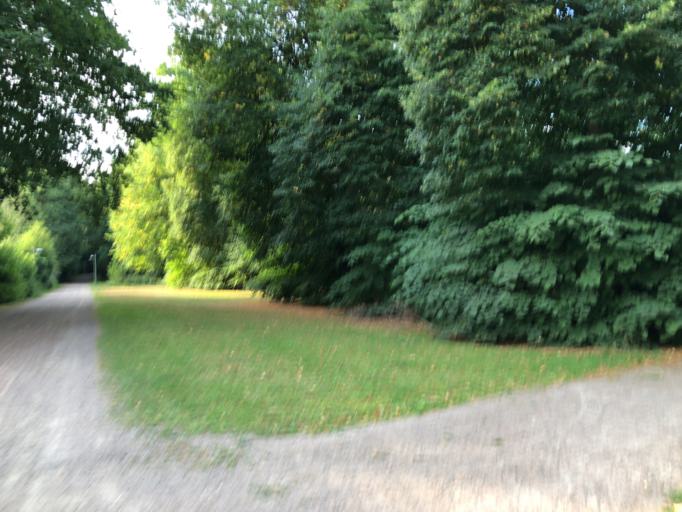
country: SE
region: Skane
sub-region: Helsingborg
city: Helsingborg
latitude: 56.0556
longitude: 12.7098
